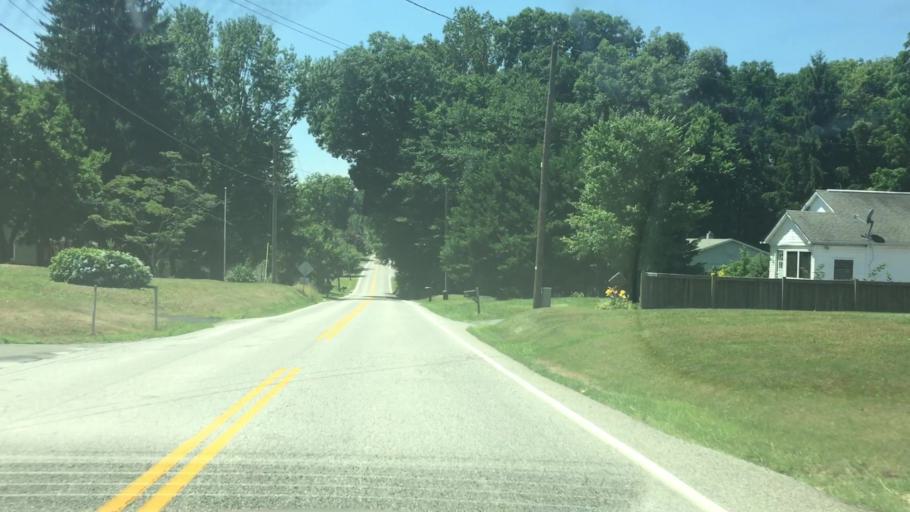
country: US
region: Maryland
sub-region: Cecil County
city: Rising Sun
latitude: 39.6750
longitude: -76.0678
